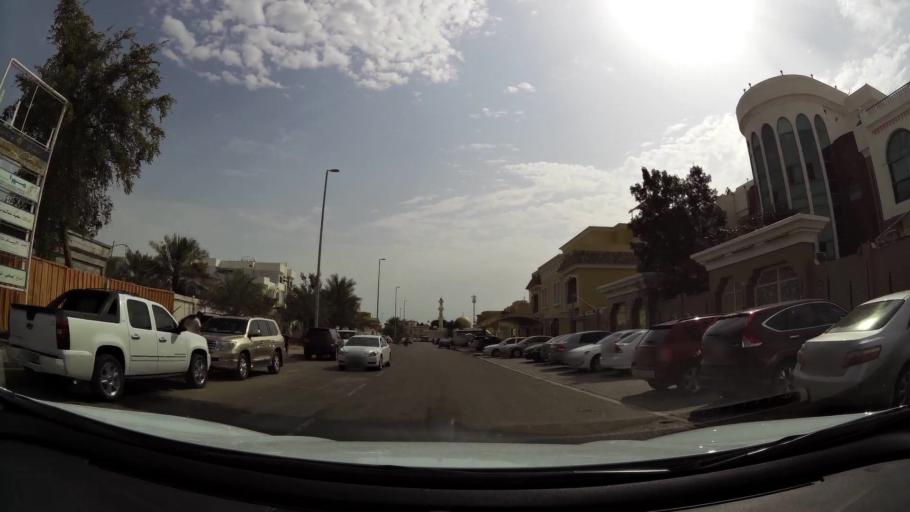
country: AE
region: Abu Dhabi
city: Abu Dhabi
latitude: 24.4423
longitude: 54.4221
